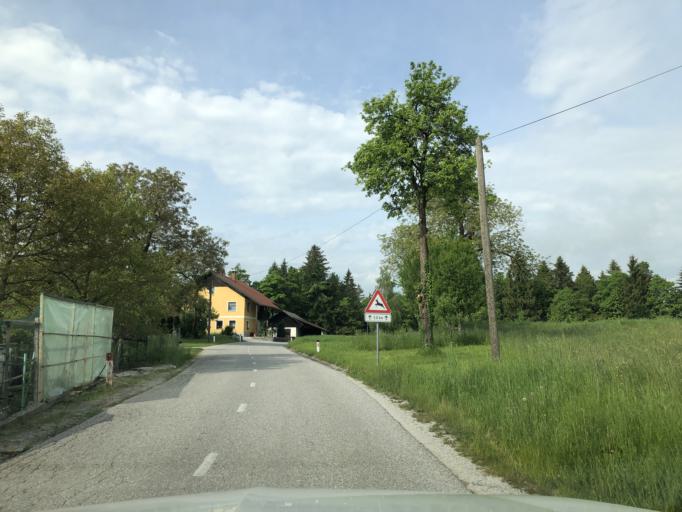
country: SI
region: Velike Lasce
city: Velike Lasce
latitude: 45.8090
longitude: 14.6257
